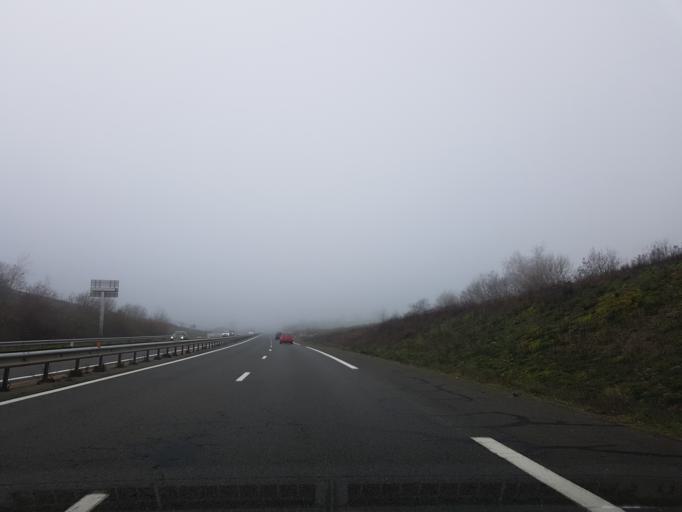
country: FR
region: Bourgogne
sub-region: Departement de Saone-et-Loire
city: Ecuisses
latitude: 46.7441
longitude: 4.5441
